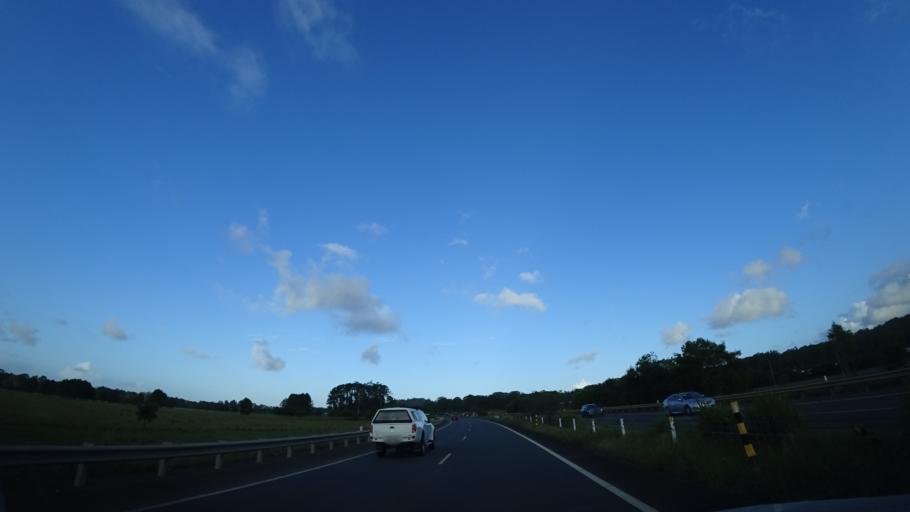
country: AU
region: Queensland
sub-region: Sunshine Coast
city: Buderim
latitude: -26.6716
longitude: 153.0138
